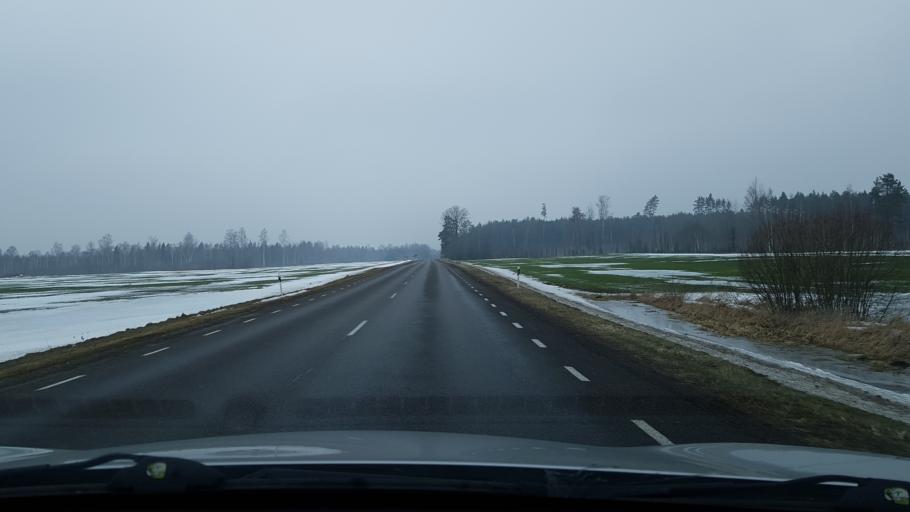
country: EE
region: Valgamaa
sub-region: Torva linn
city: Torva
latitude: 58.1088
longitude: 26.0055
